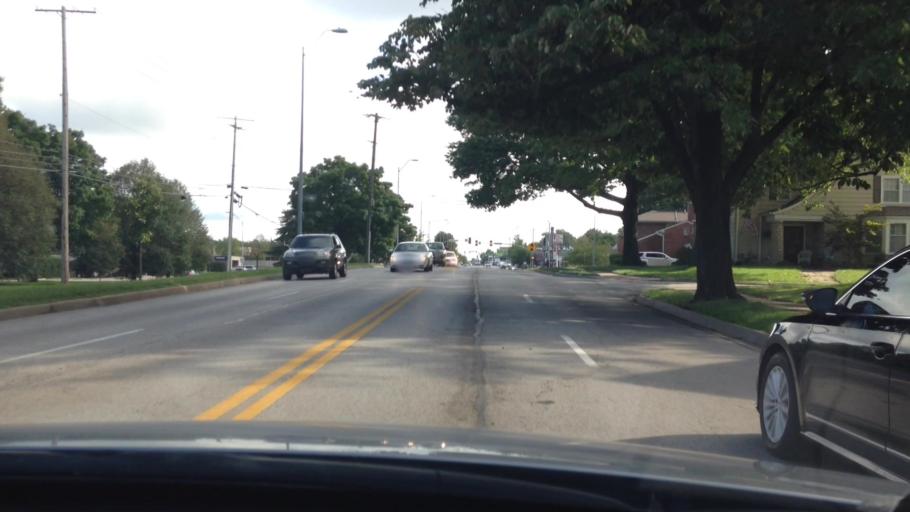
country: US
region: Kansas
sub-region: Johnson County
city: Mission Hills
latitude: 39.0015
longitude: -94.5937
